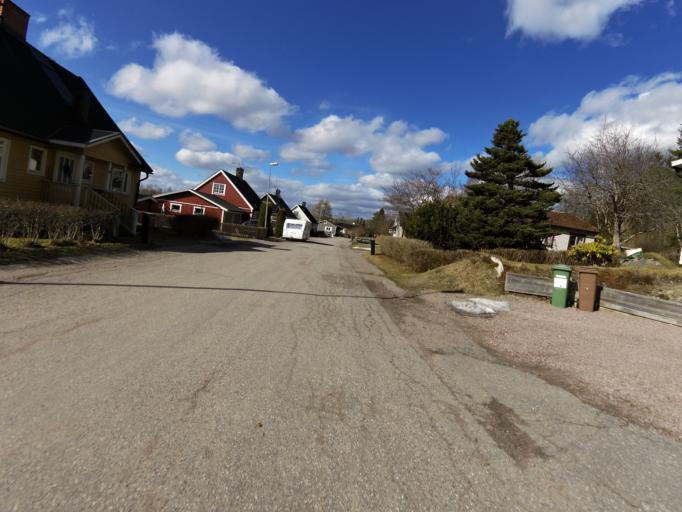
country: SE
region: Gaevleborg
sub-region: Hofors Kommun
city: Hofors
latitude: 60.5402
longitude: 16.3152
